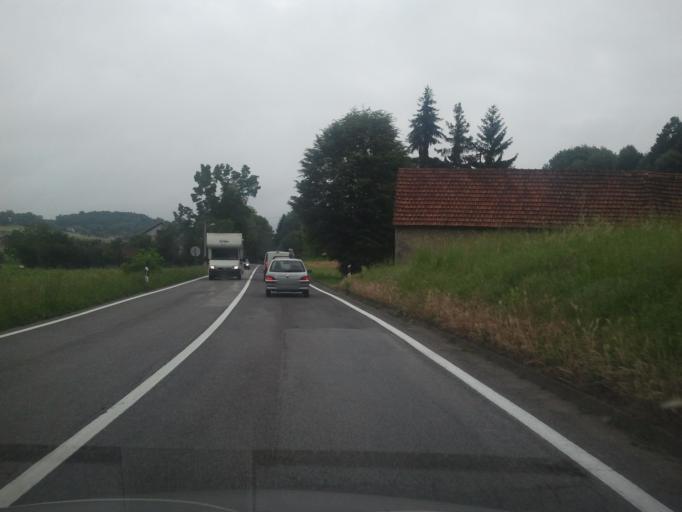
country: HR
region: Karlovacka
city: Vojnic
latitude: 45.3428
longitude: 15.6095
